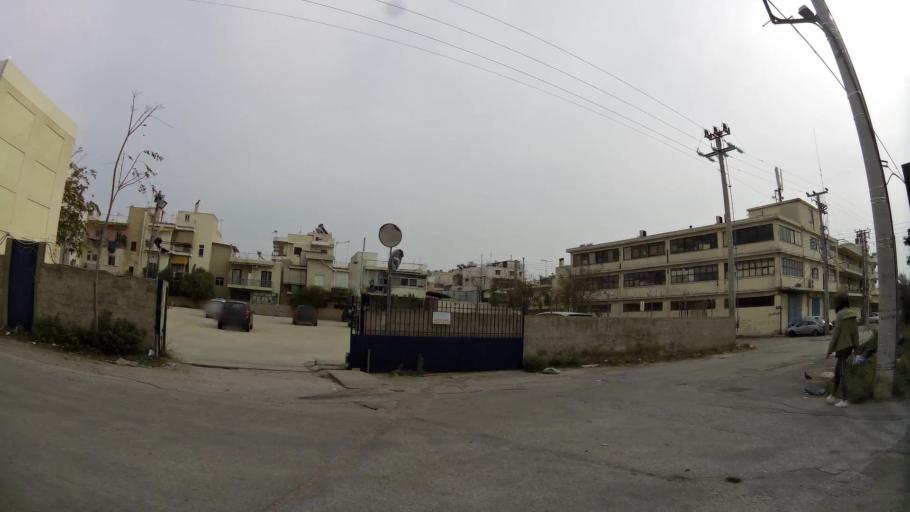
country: GR
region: Attica
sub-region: Nomarchia Athinas
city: Tavros
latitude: 37.9743
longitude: 23.6907
